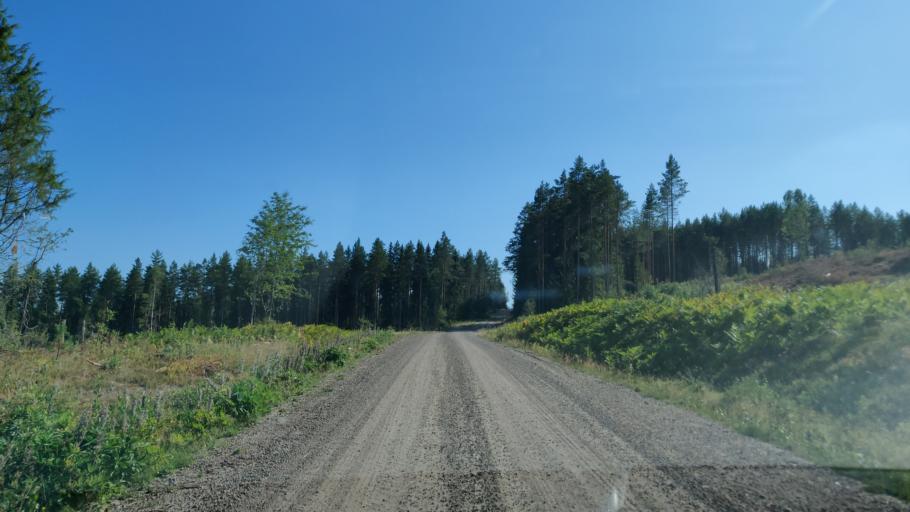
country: SE
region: Vaermland
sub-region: Hagfors Kommun
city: Ekshaerad
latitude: 60.1467
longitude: 13.5165
